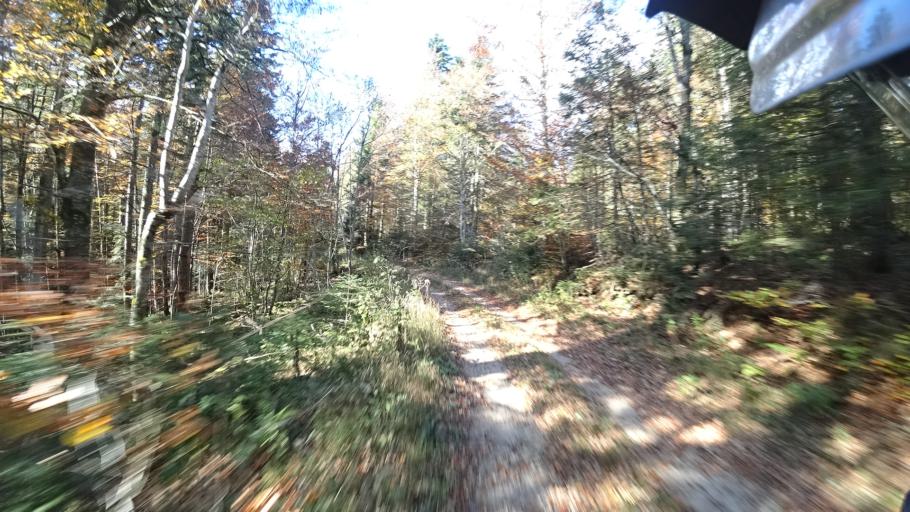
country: HR
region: Karlovacka
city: Plaski
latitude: 45.0427
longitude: 15.3402
